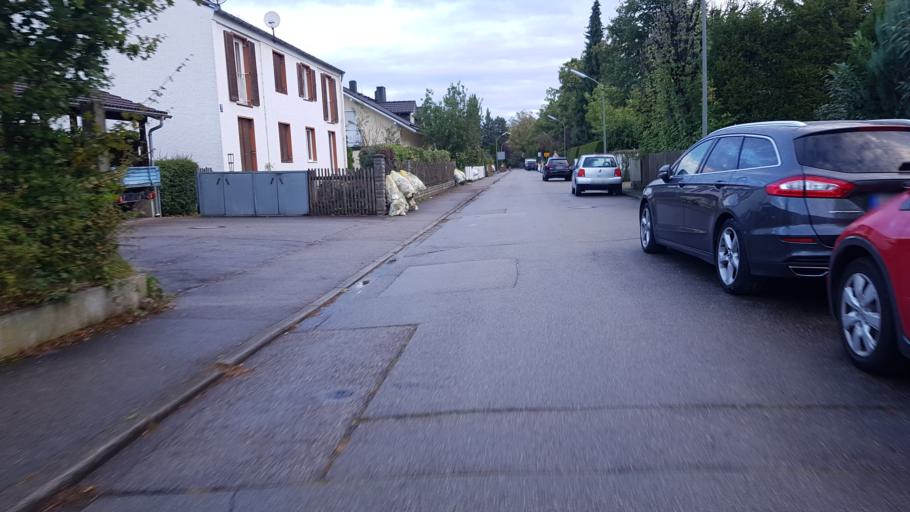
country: DE
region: Bavaria
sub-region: Upper Bavaria
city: Neubiberg
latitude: 48.0775
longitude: 11.6741
